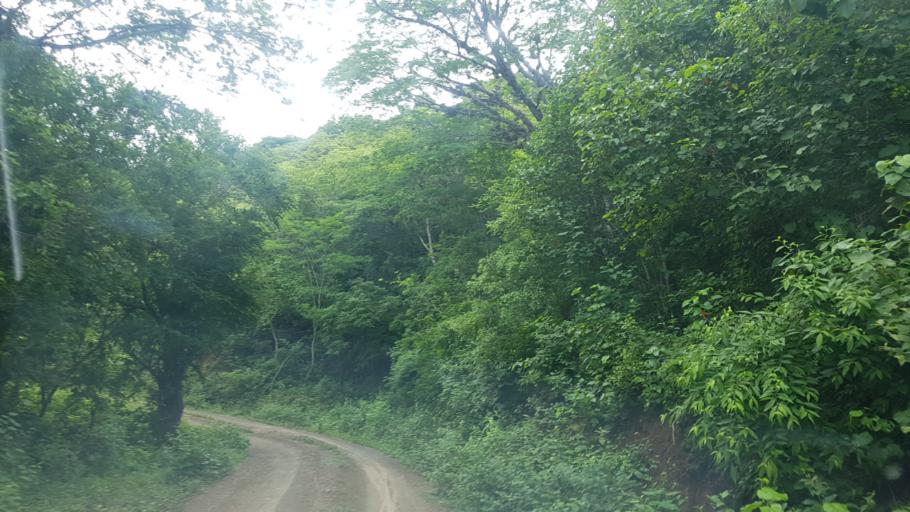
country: NI
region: Nueva Segovia
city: Mozonte
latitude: 13.5864
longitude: -86.3959
